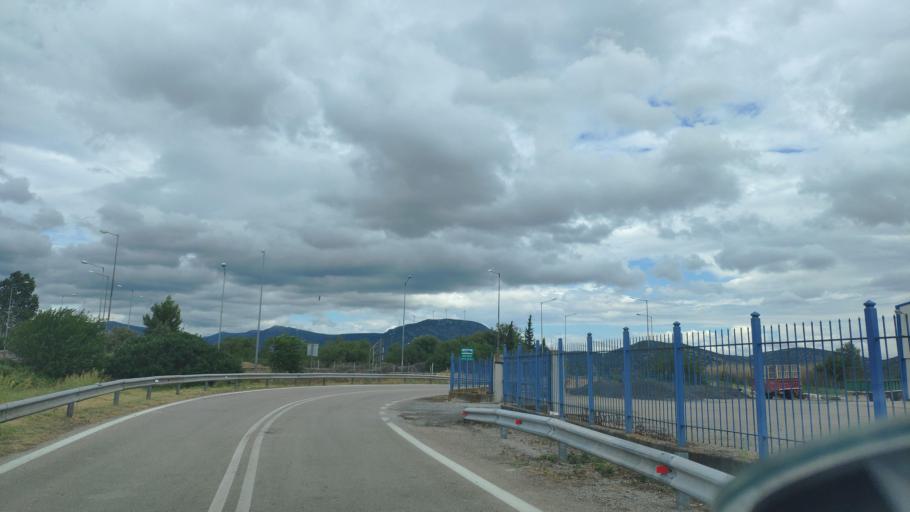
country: GR
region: Central Greece
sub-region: Nomos Voiotias
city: Akraifnia
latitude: 38.4885
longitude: 23.1607
